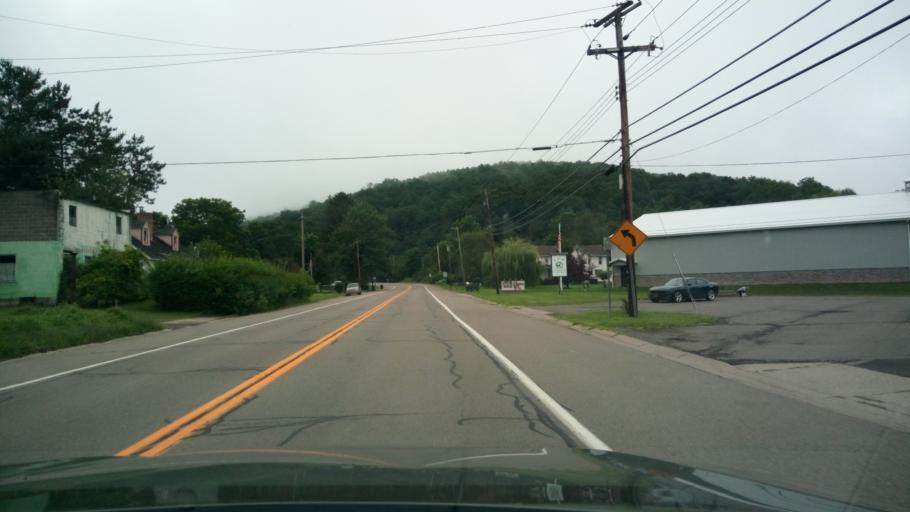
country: US
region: New York
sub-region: Chemung County
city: West Elmira
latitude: 42.0817
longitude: -76.8806
